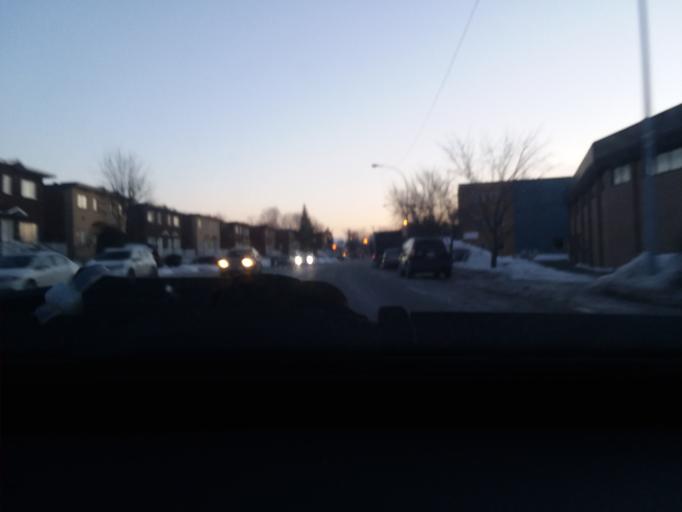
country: CA
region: Quebec
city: Montreal-Ouest
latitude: 45.4357
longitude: -73.6371
